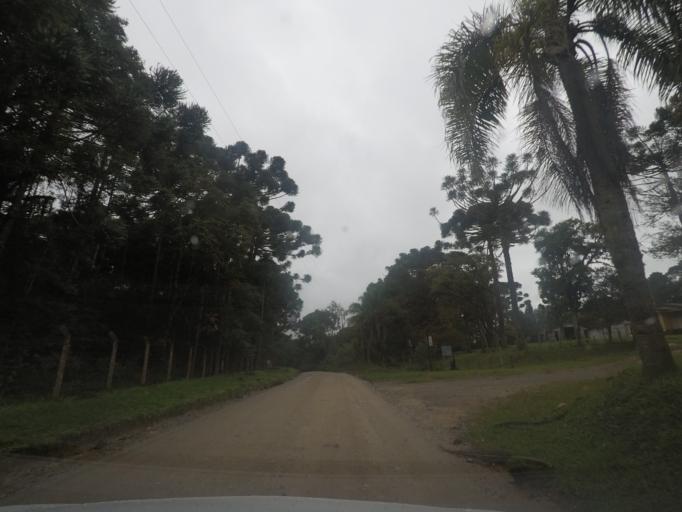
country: BR
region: Parana
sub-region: Campina Grande Do Sul
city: Campina Grande do Sul
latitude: -25.3086
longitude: -49.0980
